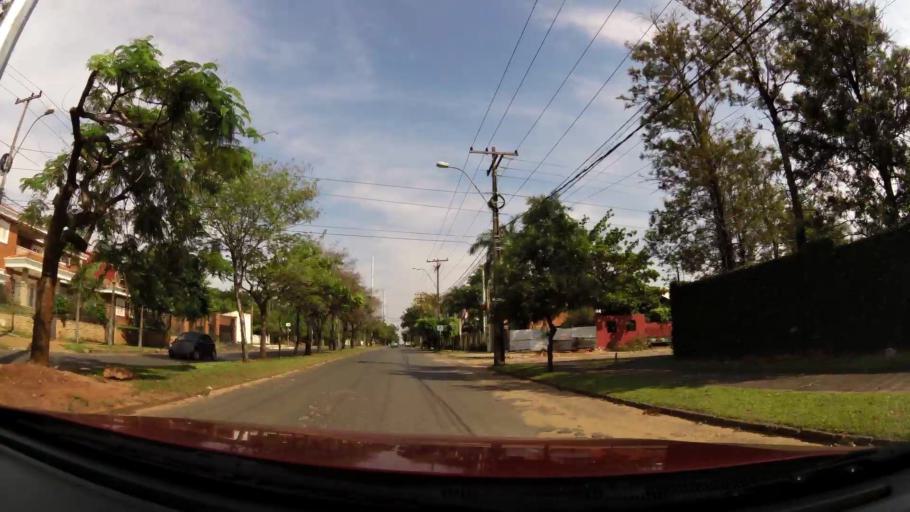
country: PY
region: Central
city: Fernando de la Mora
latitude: -25.2657
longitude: -57.5537
